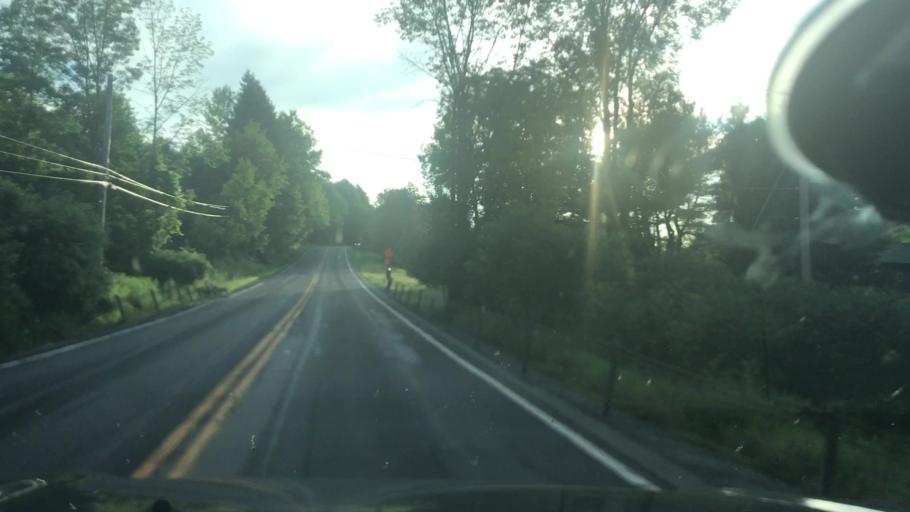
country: US
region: New York
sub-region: Otsego County
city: Unadilla
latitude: 42.3384
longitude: -75.2467
